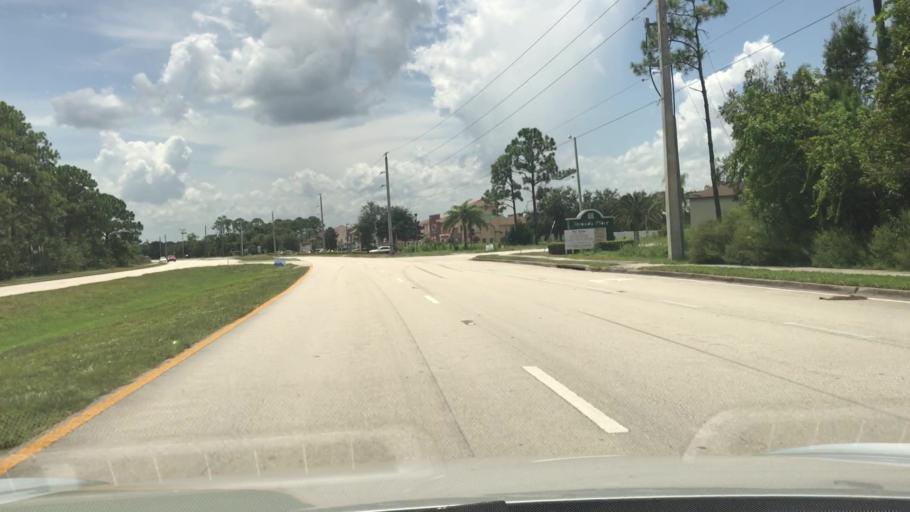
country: US
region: Florida
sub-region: Brevard County
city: June Park
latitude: 28.1263
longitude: -80.6831
